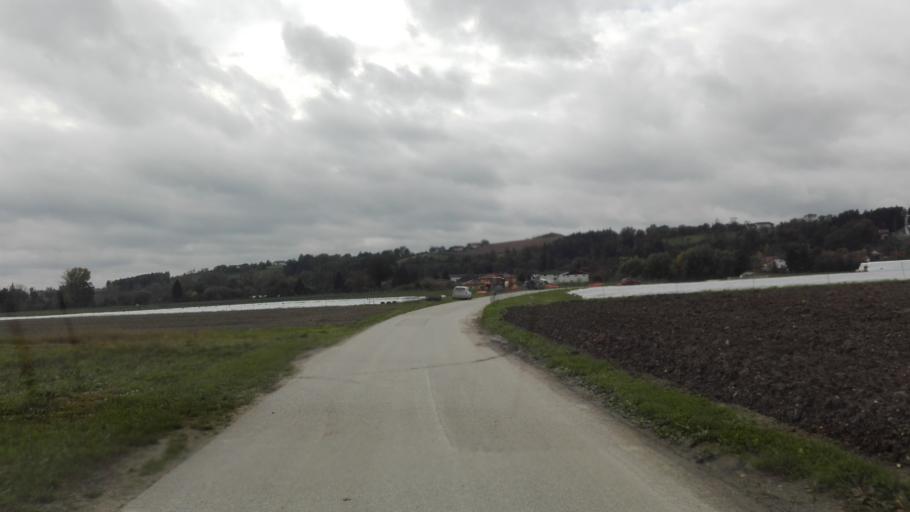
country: AT
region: Upper Austria
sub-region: Politischer Bezirk Urfahr-Umgebung
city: Feldkirchen an der Donau
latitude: 48.3266
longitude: 14.0066
